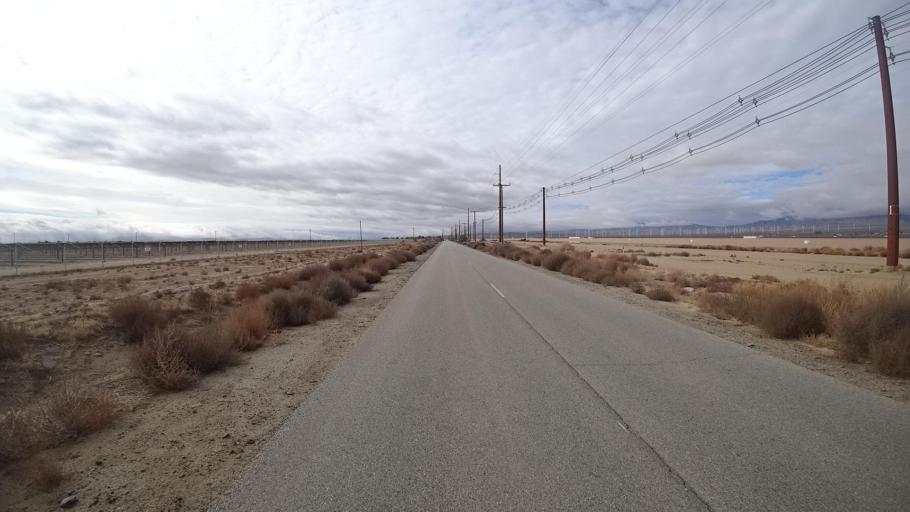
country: US
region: California
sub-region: Kern County
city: Rosamond
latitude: 34.8630
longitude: -118.3682
